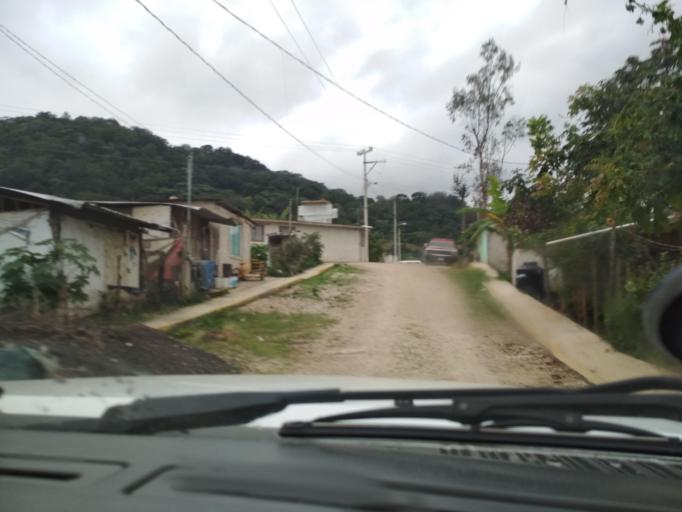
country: MX
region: Veracruz
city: El Castillo
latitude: 19.5719
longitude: -96.8520
